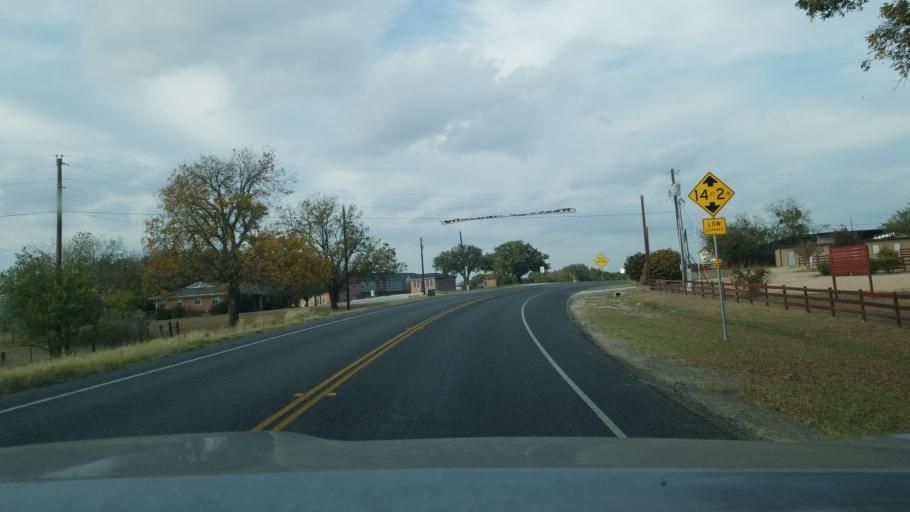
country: US
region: Texas
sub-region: Mills County
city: Goldthwaite
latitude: 31.4629
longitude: -98.5744
